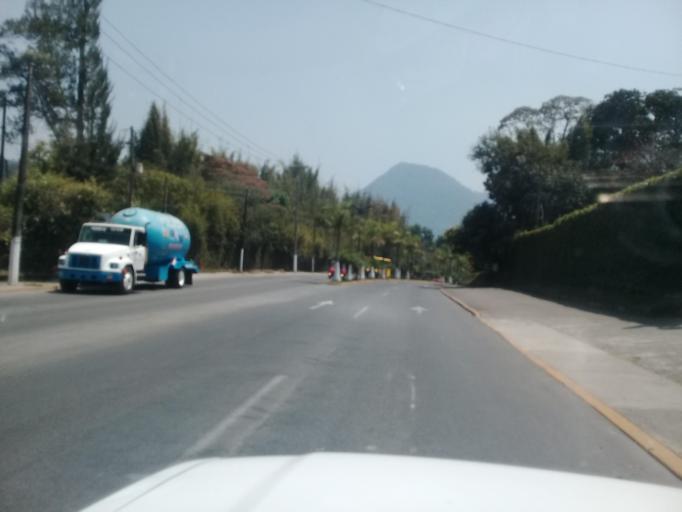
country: MX
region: Veracruz
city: Ixtac Zoquitlan
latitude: 18.8613
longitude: -97.0416
